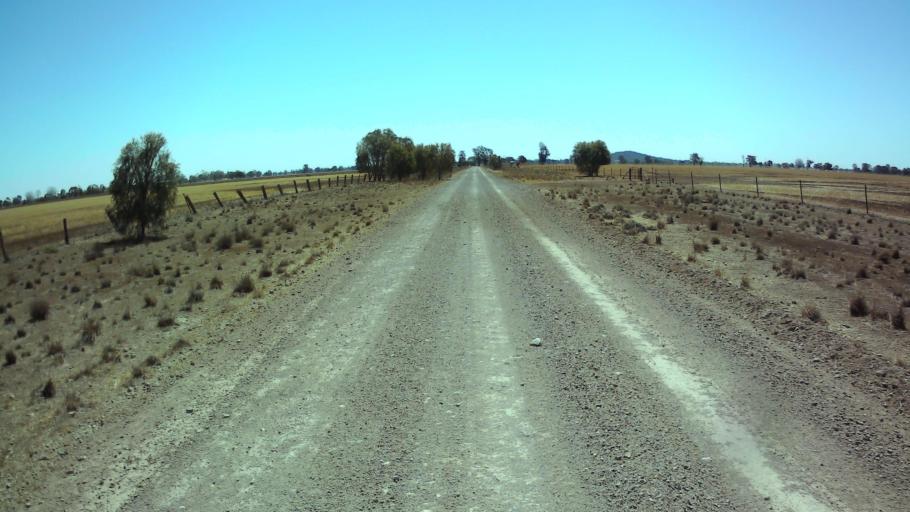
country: AU
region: New South Wales
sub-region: Forbes
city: Forbes
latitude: -33.7467
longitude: 147.7215
